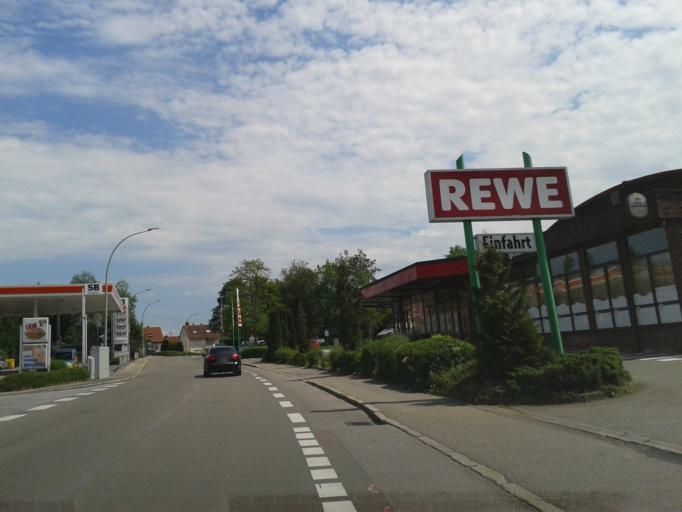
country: DE
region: Baden-Wuerttemberg
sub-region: Regierungsbezirk Stuttgart
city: Murrhardt
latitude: 48.9830
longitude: 9.5596
